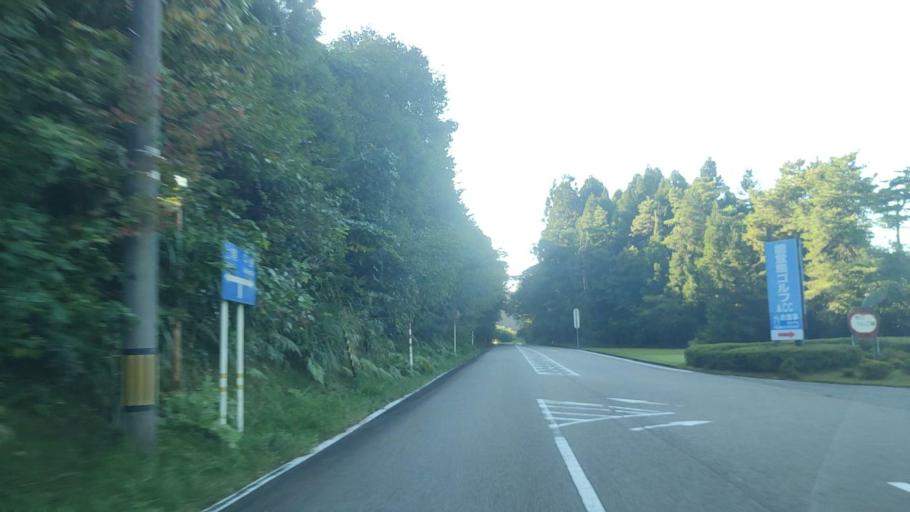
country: JP
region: Ishikawa
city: Nanao
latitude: 37.1181
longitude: 136.9606
